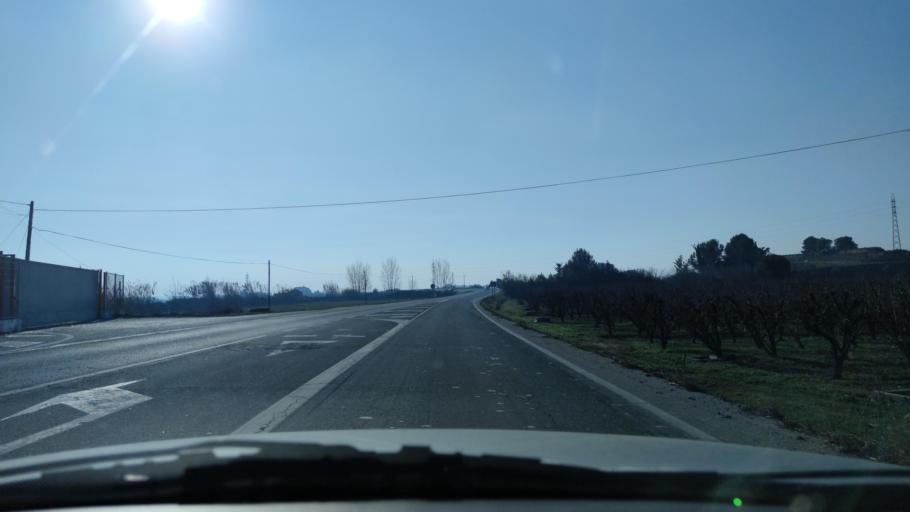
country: ES
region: Catalonia
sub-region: Provincia de Lleida
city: Torrefarrera
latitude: 41.6603
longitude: 0.6311
